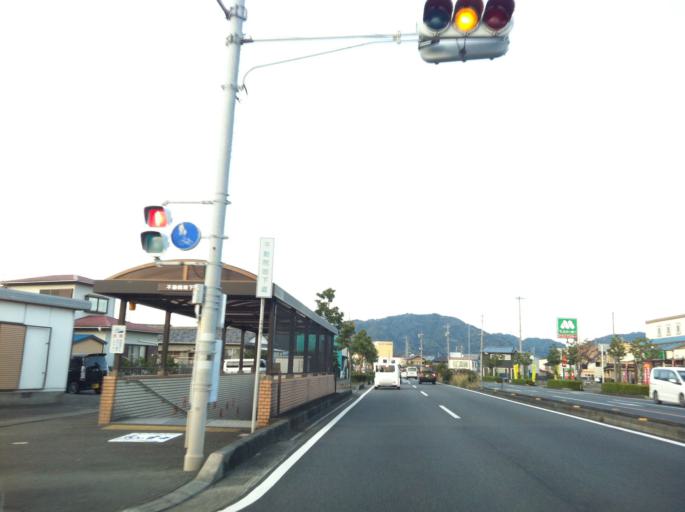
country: JP
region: Shizuoka
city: Yaizu
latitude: 34.8572
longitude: 138.3007
